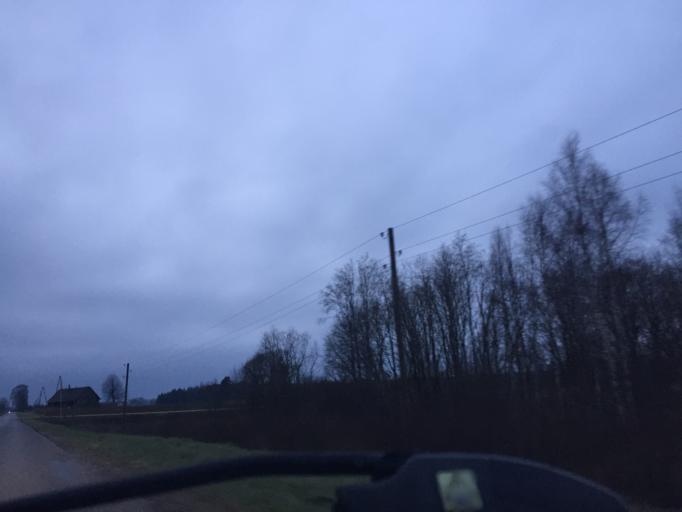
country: LV
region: Aloja
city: Aloja
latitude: 57.6267
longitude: 24.8561
